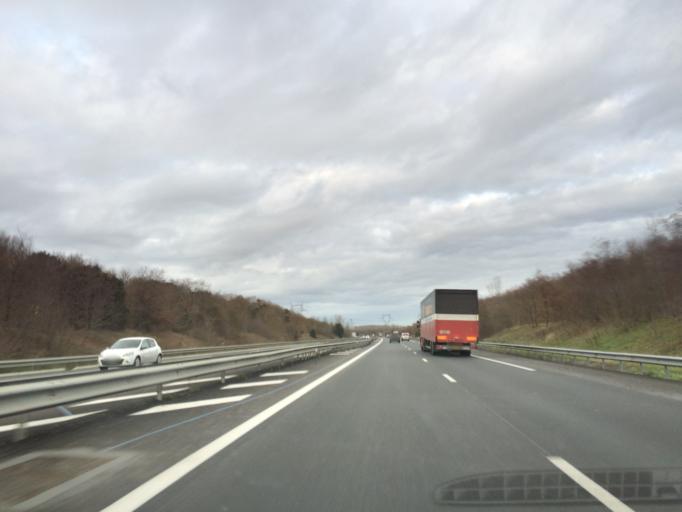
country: FR
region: Poitou-Charentes
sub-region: Departement des Deux-Sevres
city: Fors
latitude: 46.2430
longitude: -0.4314
